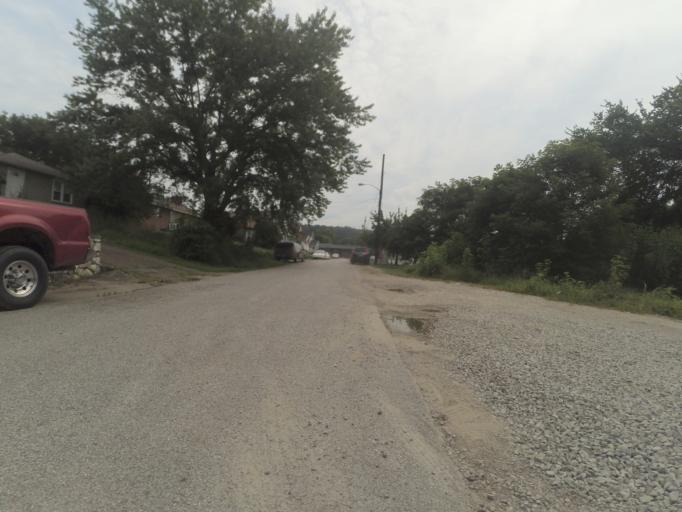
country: US
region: West Virginia
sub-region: Cabell County
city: Huntington
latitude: 38.4290
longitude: -82.4584
